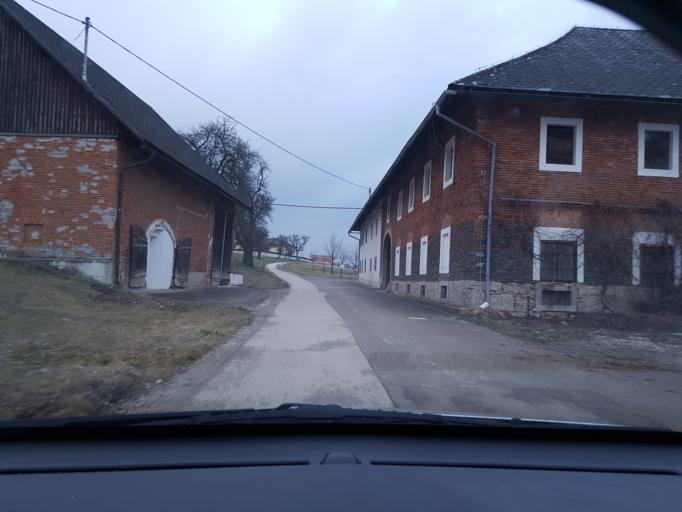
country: AT
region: Upper Austria
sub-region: Politischer Bezirk Linz-Land
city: Ansfelden
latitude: 48.1581
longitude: 14.3298
